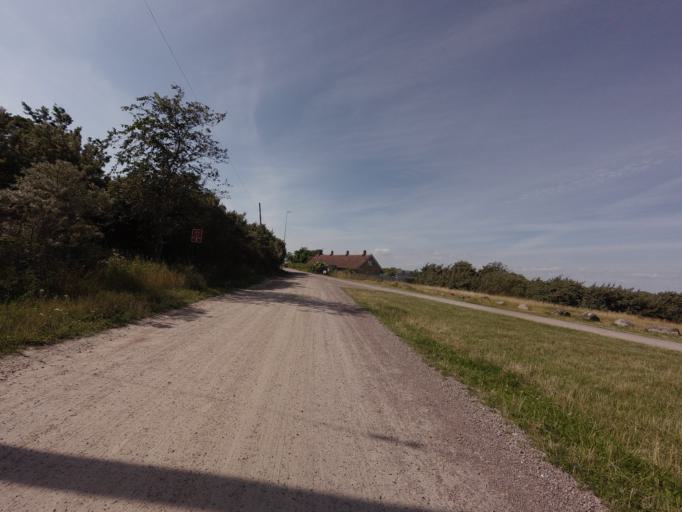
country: SE
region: Skane
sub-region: Helsingborg
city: Rydeback
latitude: 55.9655
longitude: 12.7589
